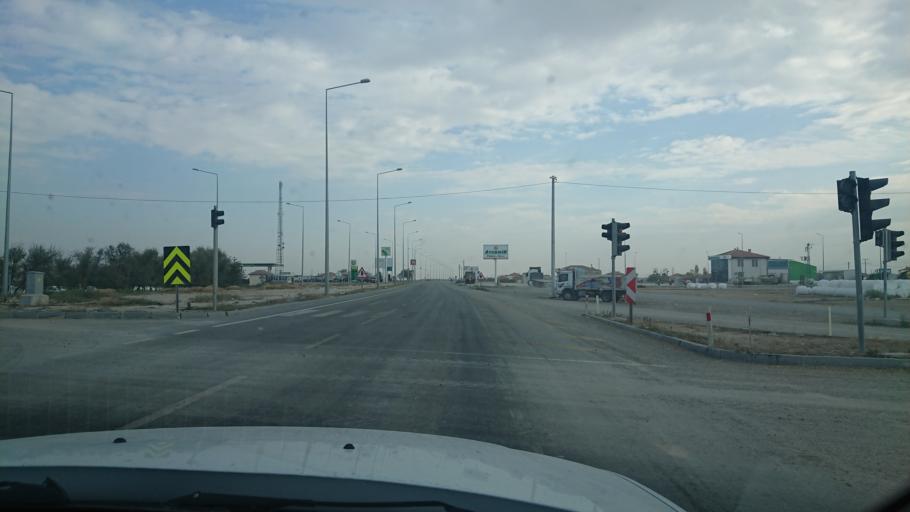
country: TR
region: Aksaray
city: Yesilova
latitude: 38.2910
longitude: 33.7605
